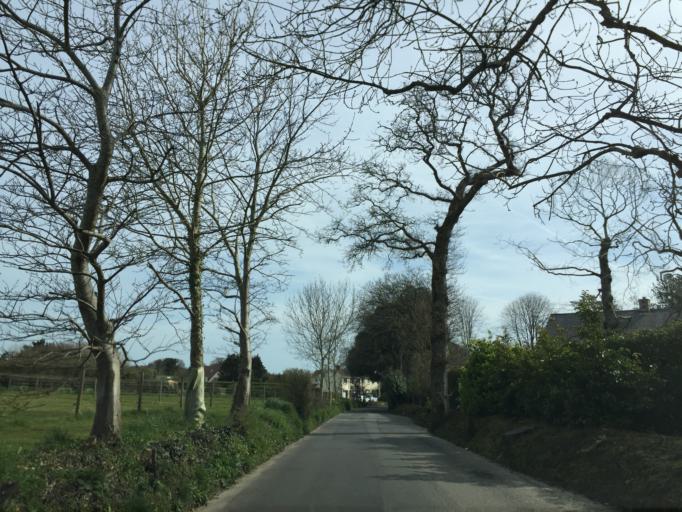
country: JE
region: St Helier
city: Saint Helier
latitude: 49.2290
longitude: -2.1126
